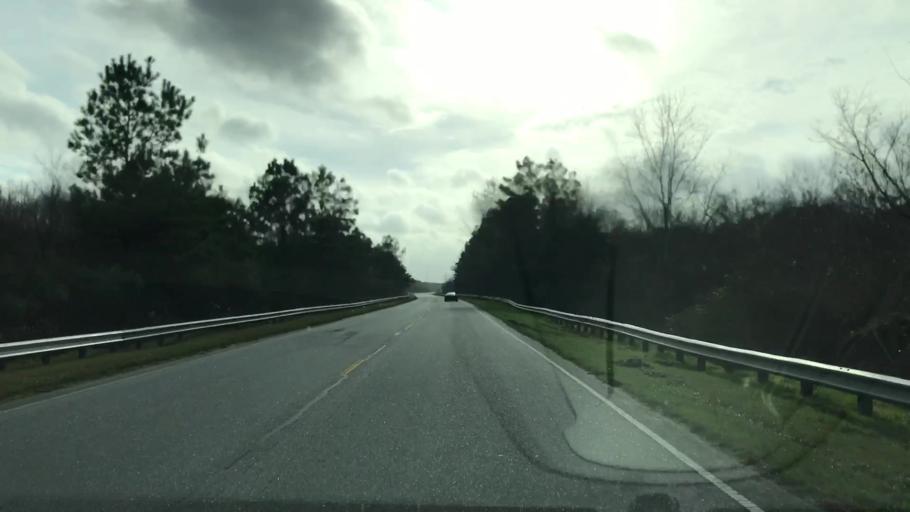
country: US
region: South Carolina
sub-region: Williamsburg County
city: Andrews
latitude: 33.3140
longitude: -79.6704
